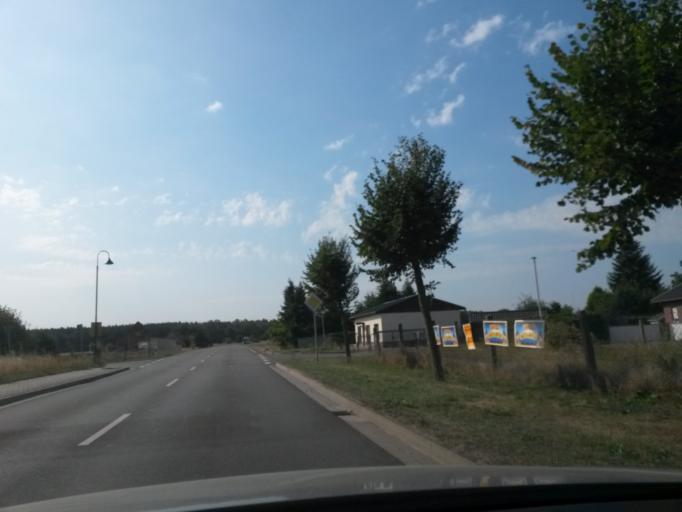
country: DE
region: Saxony-Anhalt
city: Jerichow
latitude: 52.5364
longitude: 12.0155
